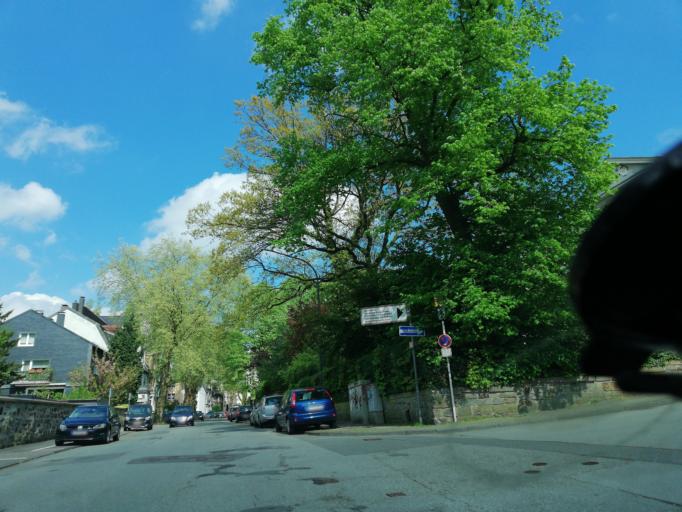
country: DE
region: North Rhine-Westphalia
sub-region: Regierungsbezirk Dusseldorf
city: Wuppertal
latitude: 51.2599
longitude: 7.1779
